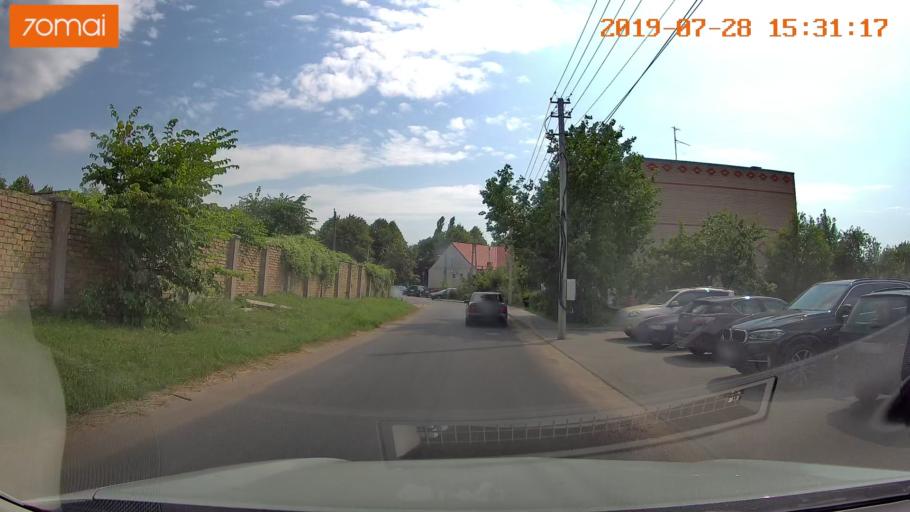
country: RU
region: Kaliningrad
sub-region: Gorod Kaliningrad
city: Yantarnyy
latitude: 54.8711
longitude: 19.9398
